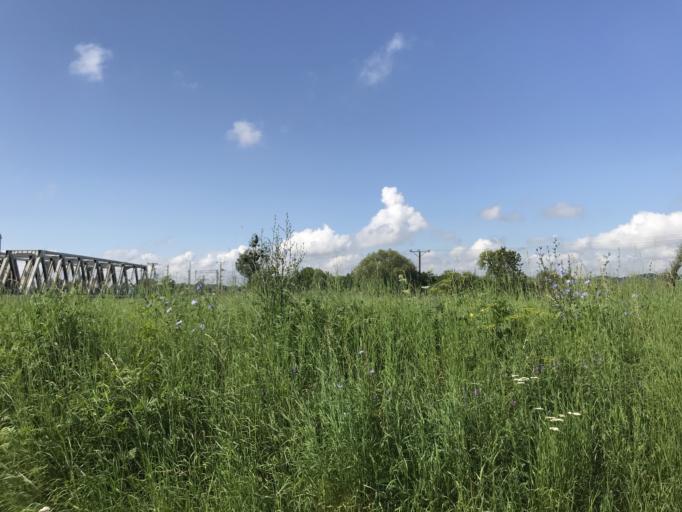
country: PL
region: Pomeranian Voivodeship
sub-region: Gdansk
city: Gdansk
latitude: 54.3258
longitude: 18.6582
